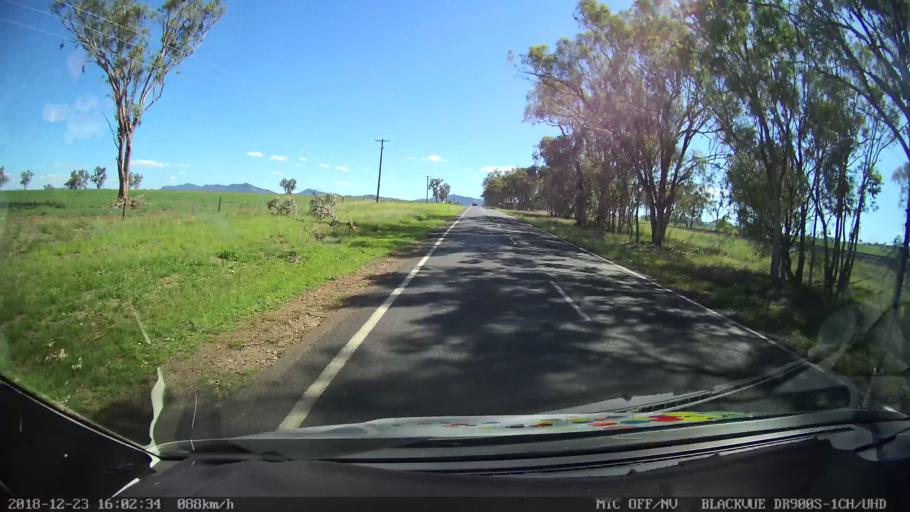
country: AU
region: New South Wales
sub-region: Tamworth Municipality
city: Phillip
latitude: -31.2337
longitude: 150.8079
